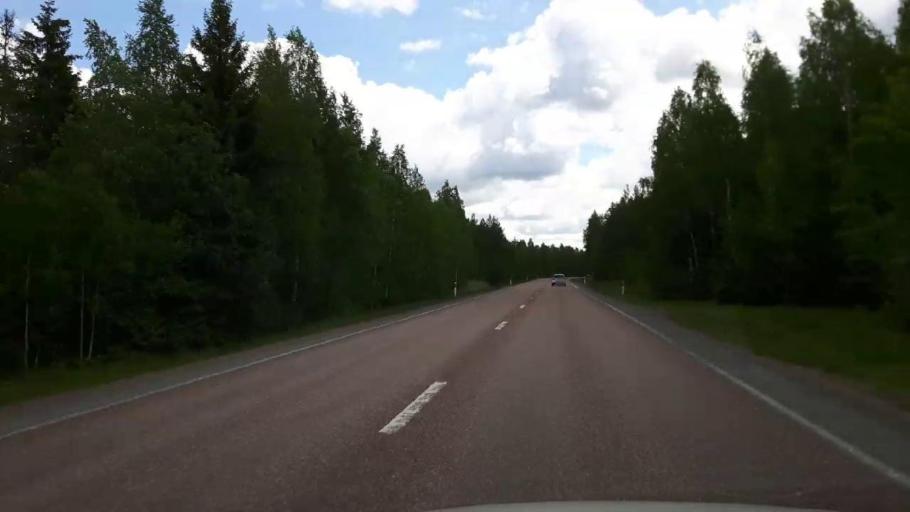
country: SE
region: Dalarna
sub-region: Saters Kommun
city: Saeter
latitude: 60.4985
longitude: 15.7513
